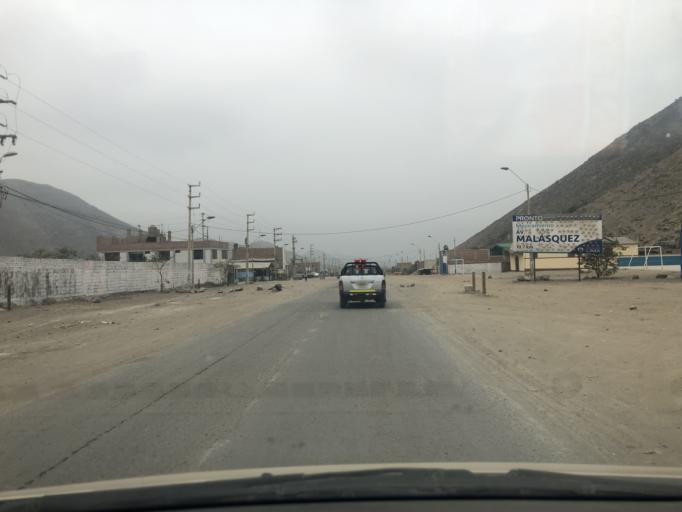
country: PE
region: Lima
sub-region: Lima
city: Cieneguilla
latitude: -12.1593
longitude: -76.8676
